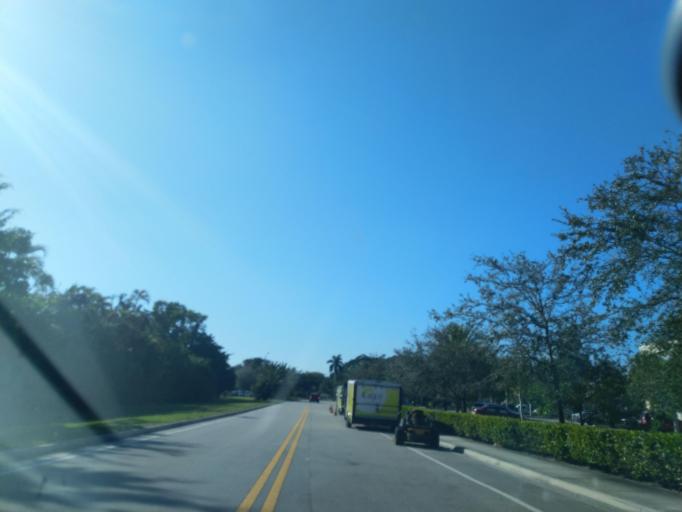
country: US
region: Florida
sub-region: Broward County
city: Davie
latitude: 26.0771
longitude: -80.2301
